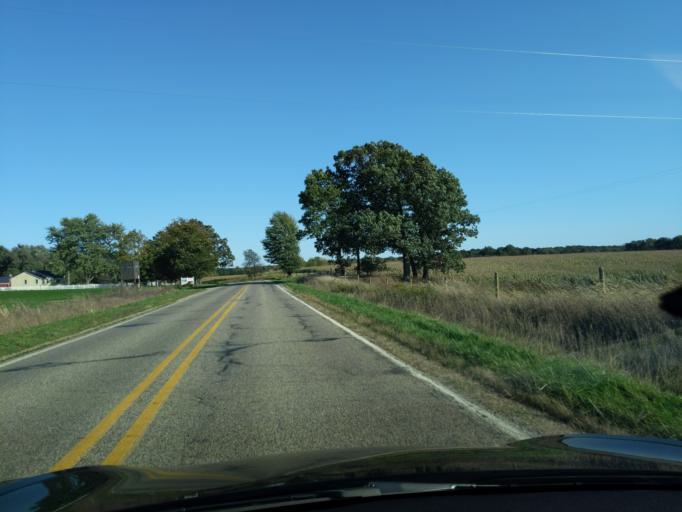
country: US
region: Michigan
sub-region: Clinton County
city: Bath
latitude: 42.9267
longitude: -84.4695
